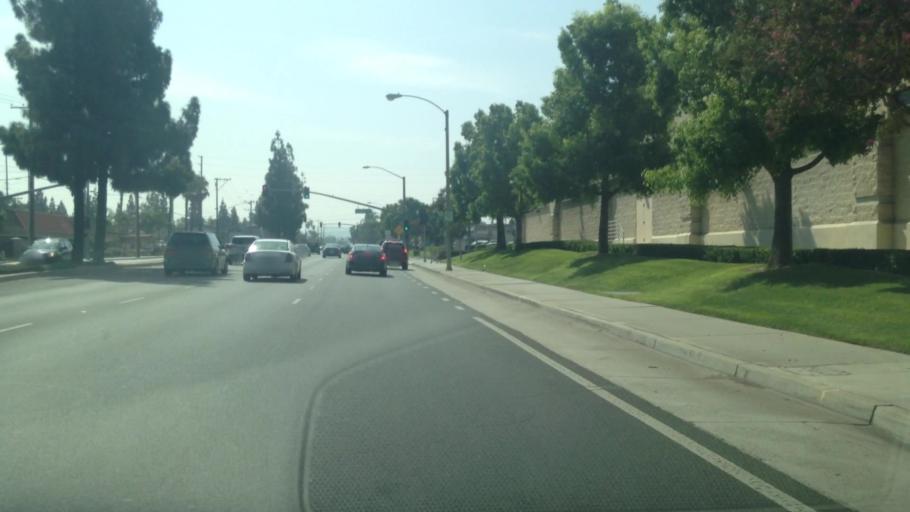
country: US
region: California
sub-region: Riverside County
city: Pedley
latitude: 33.9282
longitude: -117.4531
